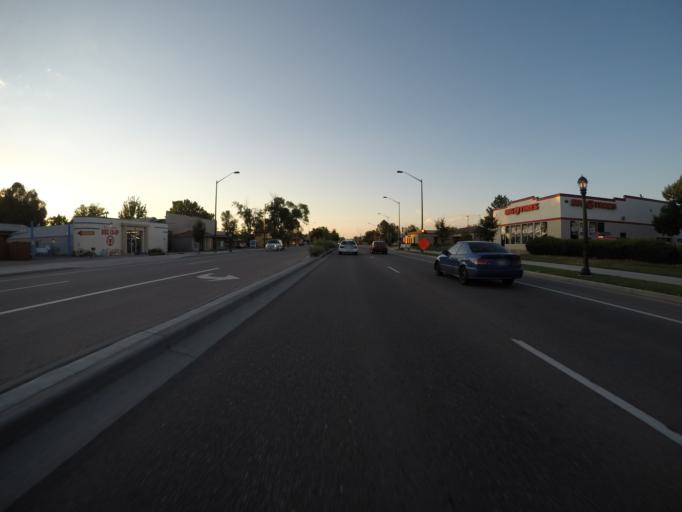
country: US
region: Colorado
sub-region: Larimer County
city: Fort Collins
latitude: 40.6074
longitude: -105.0765
